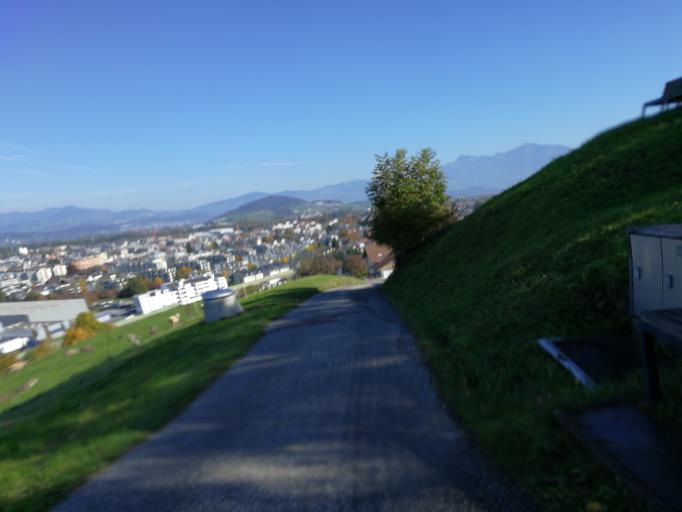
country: CH
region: Schwyz
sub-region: Bezirk March
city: Altendorf
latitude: 47.1852
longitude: 8.8420
